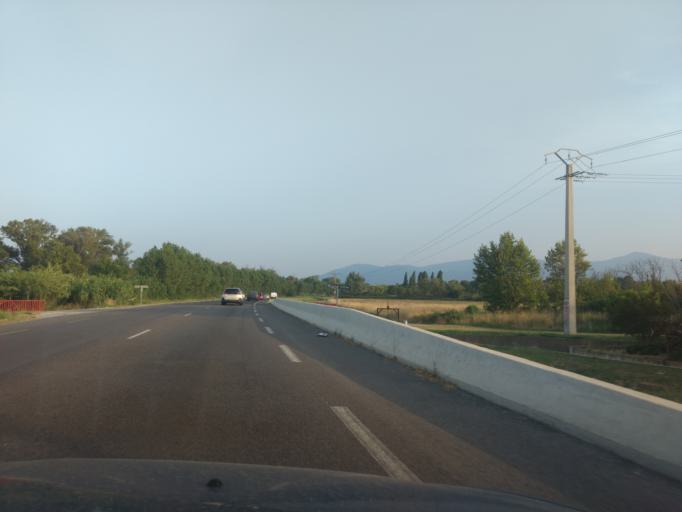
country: FR
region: Languedoc-Roussillon
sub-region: Departement des Pyrenees-Orientales
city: Saint-Cyprien-Plage
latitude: 42.6207
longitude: 3.0248
